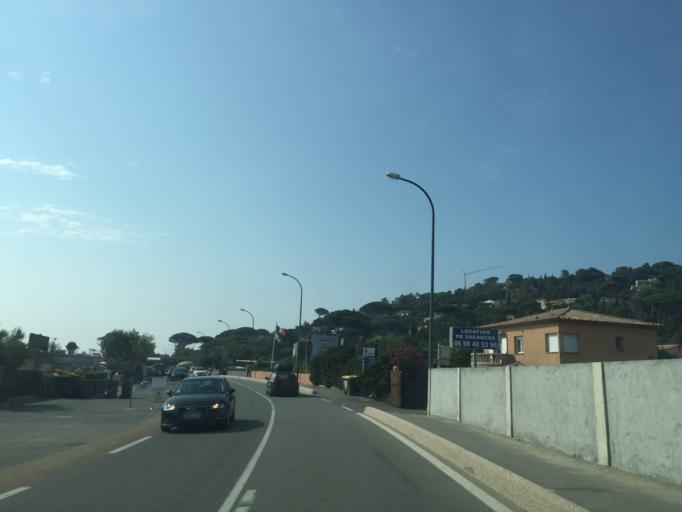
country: FR
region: Provence-Alpes-Cote d'Azur
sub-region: Departement du Var
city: Sainte-Maxime
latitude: 43.3186
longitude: 6.6651
